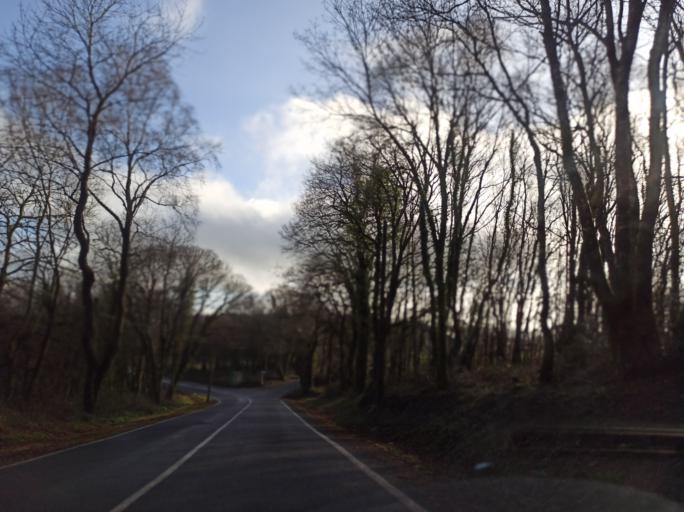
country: ES
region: Galicia
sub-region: Provincia da Coruna
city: Sobrado
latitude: 43.0787
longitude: -8.0086
